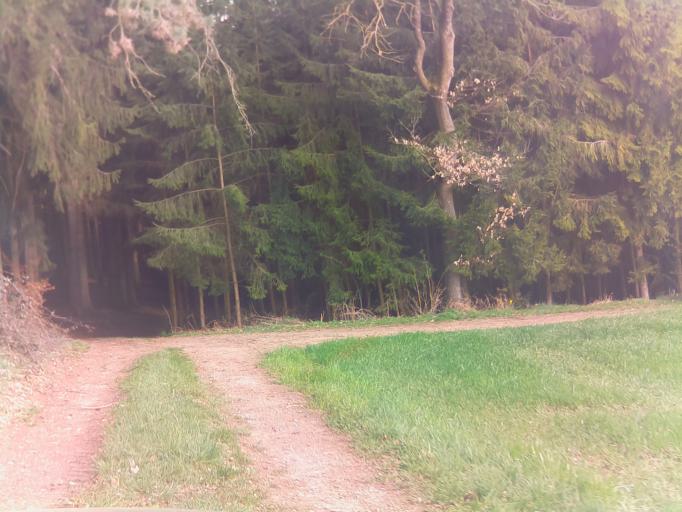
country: DE
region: Bavaria
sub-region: Swabia
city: Aindling
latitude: 48.5231
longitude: 10.9890
